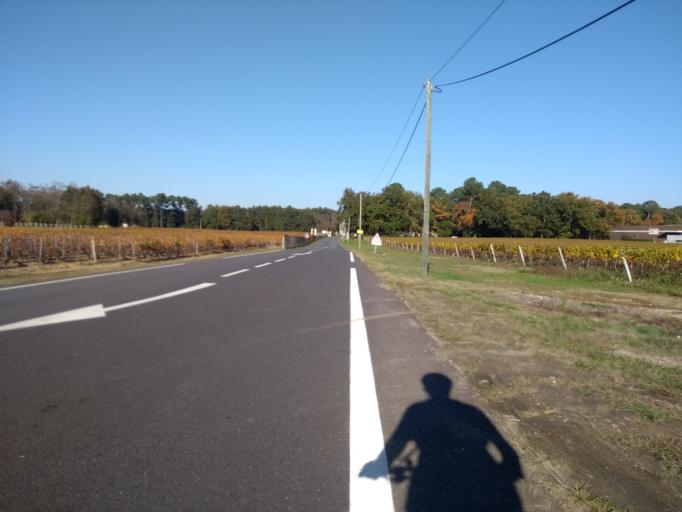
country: FR
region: Aquitaine
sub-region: Departement de la Gironde
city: Ayguemorte-les-Graves
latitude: 44.6972
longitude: -0.4823
